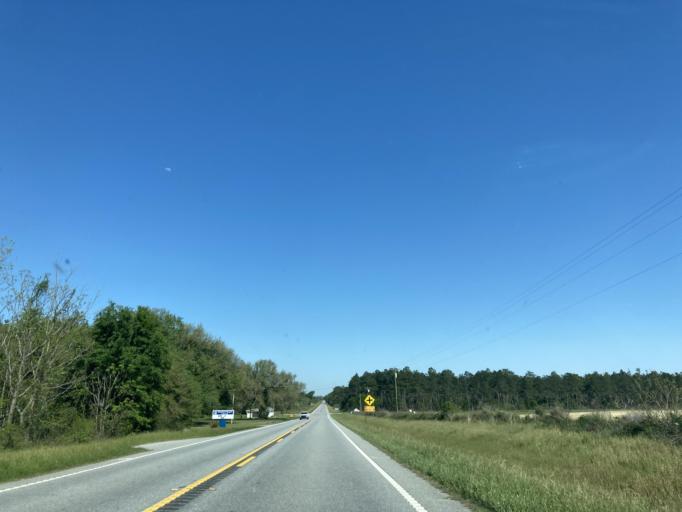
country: US
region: Georgia
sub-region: Miller County
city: Colquitt
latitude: 31.1843
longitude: -84.5729
